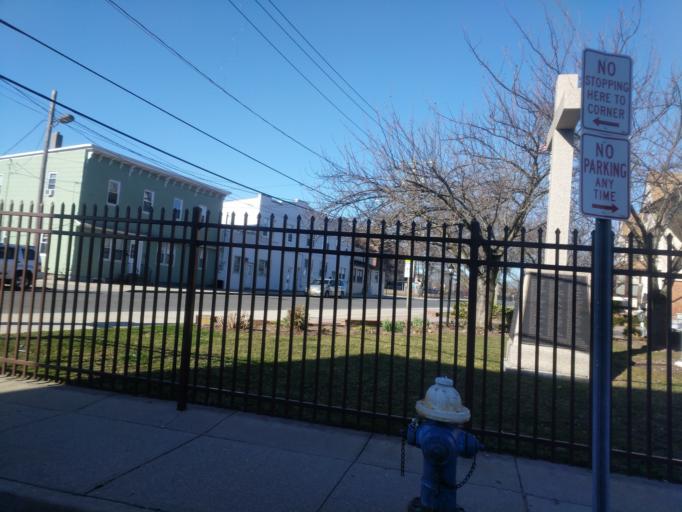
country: US
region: New York
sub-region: Nassau County
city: Inwood
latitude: 40.6164
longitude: -73.7395
